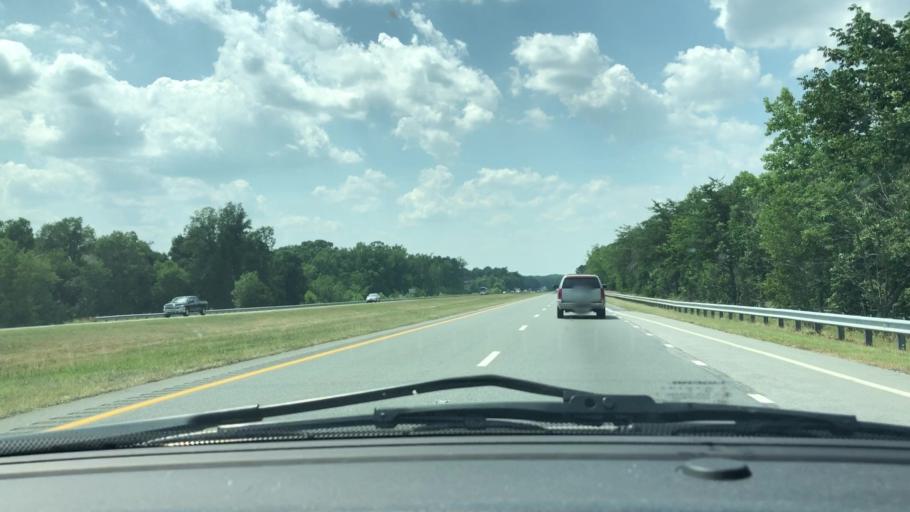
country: US
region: North Carolina
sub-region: Guilford County
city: Forest Oaks
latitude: 35.9674
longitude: -79.7113
